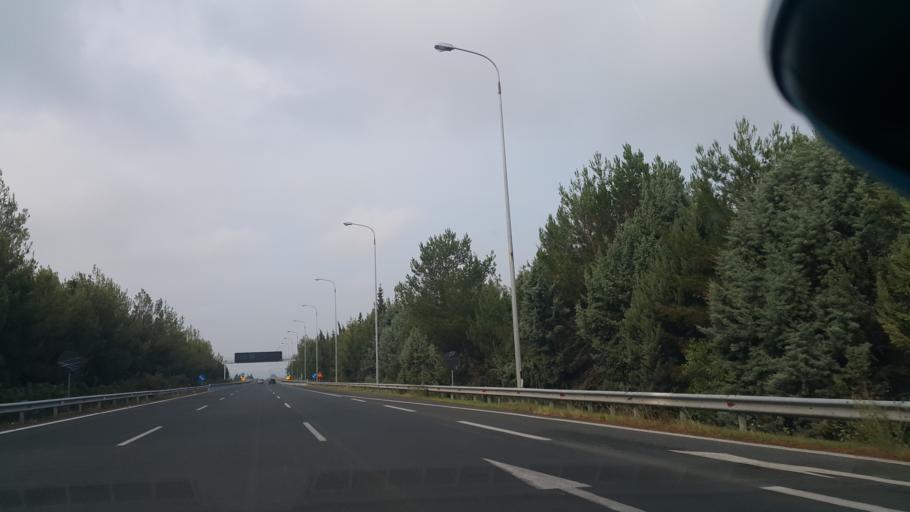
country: GR
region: Central Macedonia
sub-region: Nomos Imathias
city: Kleidi
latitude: 40.5463
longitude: 22.5899
